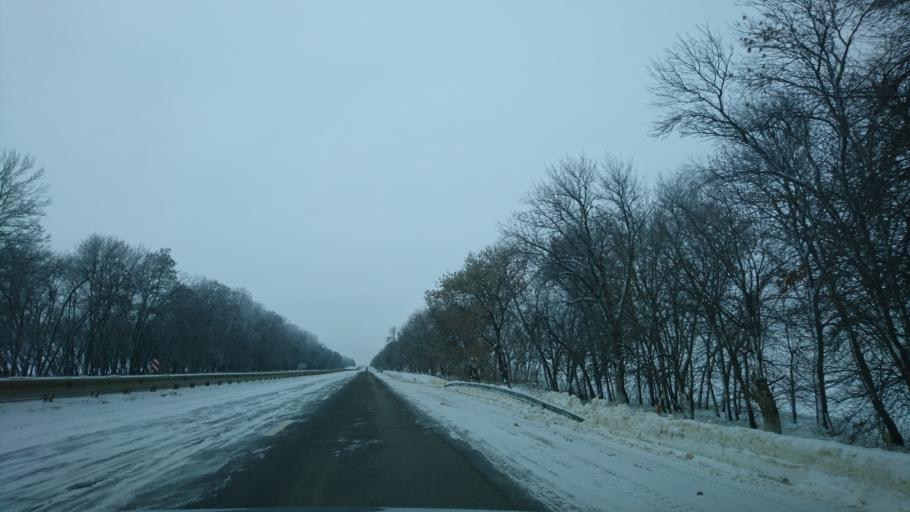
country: RU
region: Belgorod
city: Mayskiy
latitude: 50.4288
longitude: 36.3841
